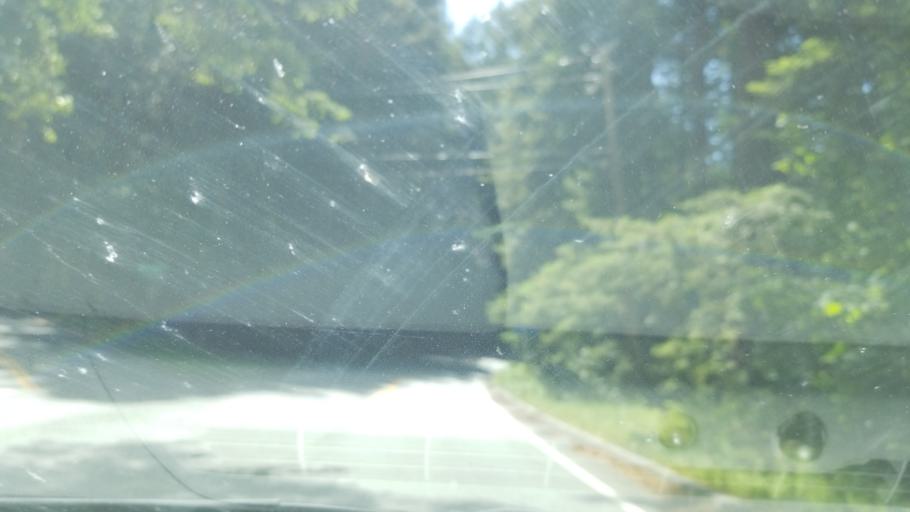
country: US
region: California
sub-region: Santa Clara County
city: Lexington Hills
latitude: 37.1161
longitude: -121.9335
